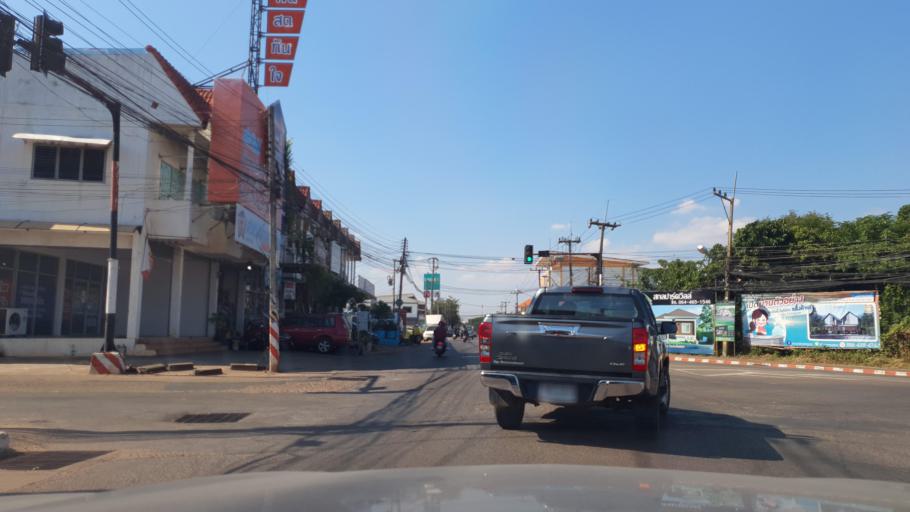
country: TH
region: Sakon Nakhon
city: Sakon Nakhon
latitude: 17.1639
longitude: 104.1235
